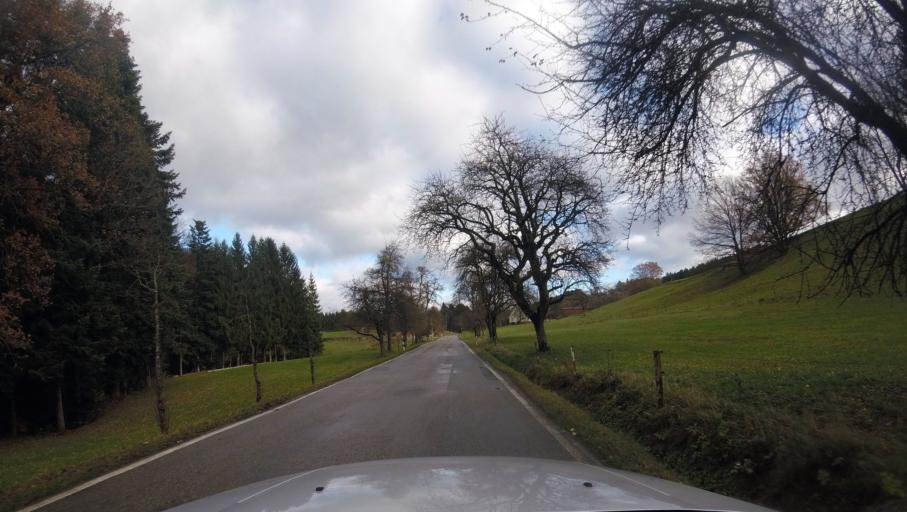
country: DE
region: Baden-Wuerttemberg
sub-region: Regierungsbezirk Stuttgart
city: Gschwend
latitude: 48.9459
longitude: 9.7076
